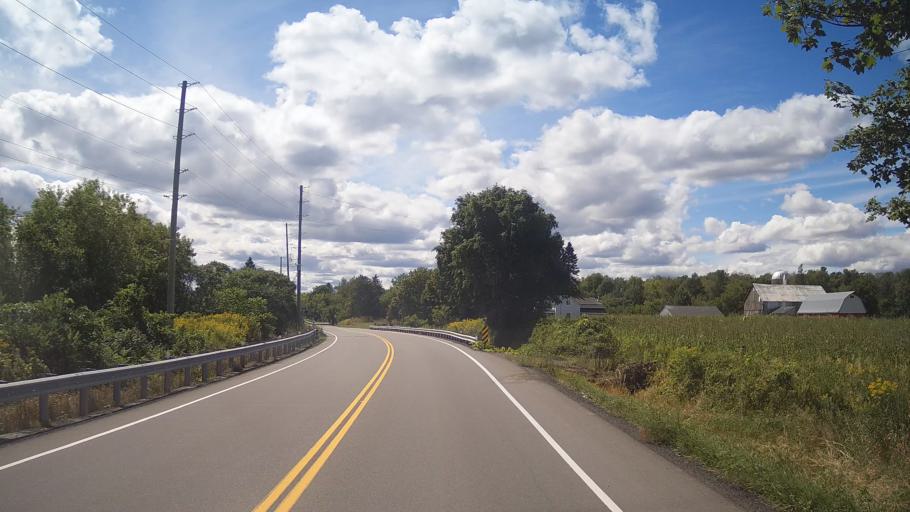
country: US
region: New York
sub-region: St. Lawrence County
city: Ogdensburg
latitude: 44.7802
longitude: -75.4216
